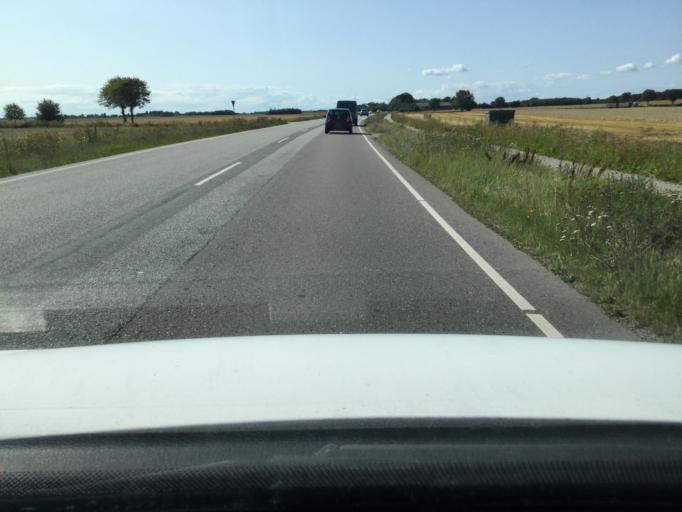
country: DK
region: Zealand
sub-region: Lolland Kommune
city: Nakskov
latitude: 54.8129
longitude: 11.1775
